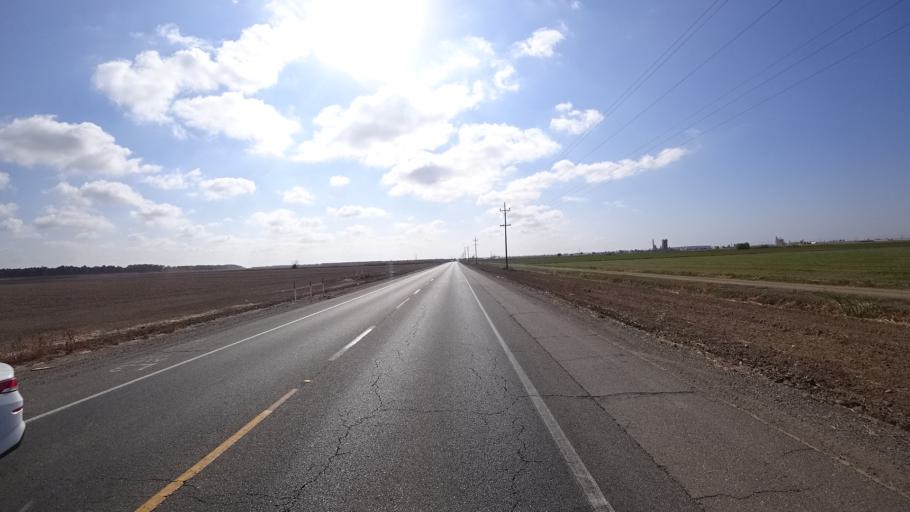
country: US
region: California
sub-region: Yolo County
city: Woodland
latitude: 38.7021
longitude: -121.7281
